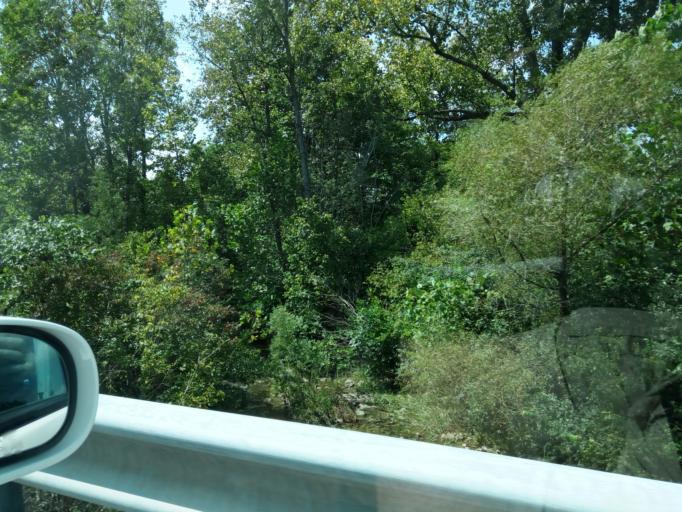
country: US
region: Kentucky
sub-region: Oldham County
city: Pewee Valley
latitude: 38.2424
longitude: -85.4602
